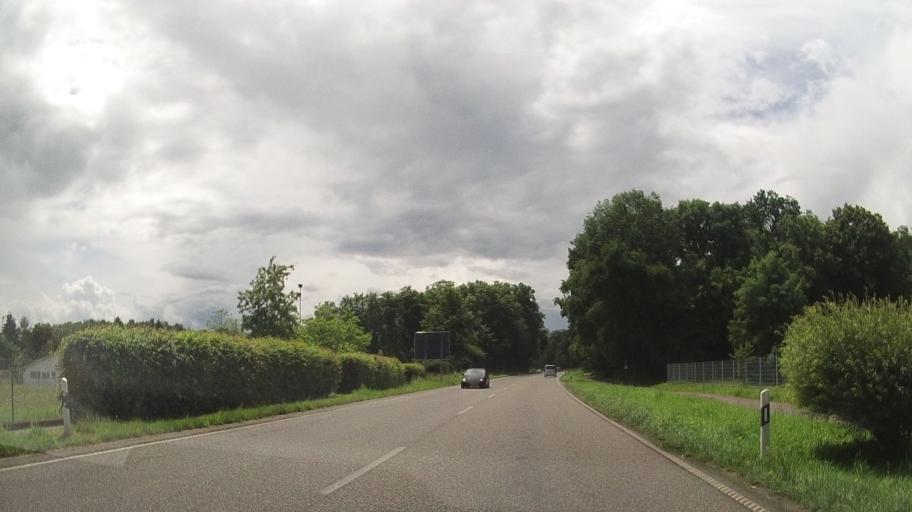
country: DE
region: Baden-Wuerttemberg
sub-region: Freiburg Region
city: Renchen
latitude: 48.5797
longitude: 8.0019
